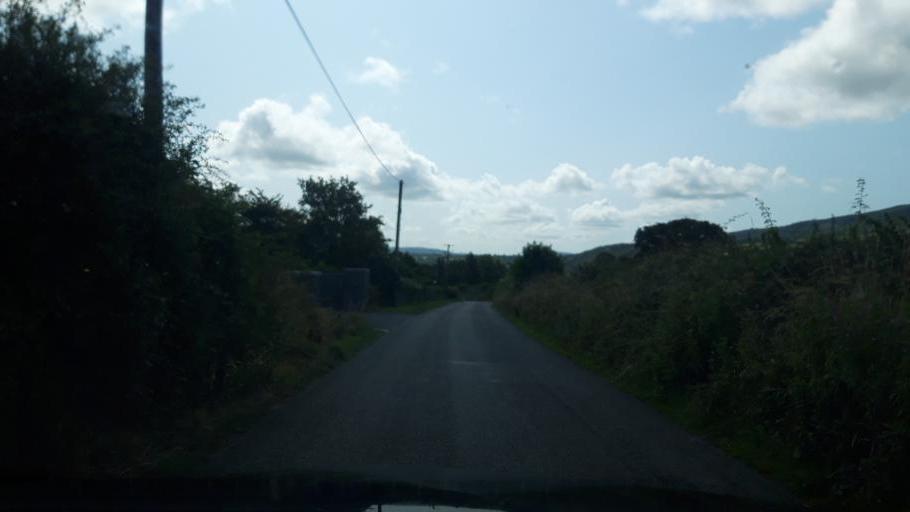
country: IE
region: Leinster
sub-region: Kilkenny
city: Graiguenamanagh
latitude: 52.5488
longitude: -6.9696
